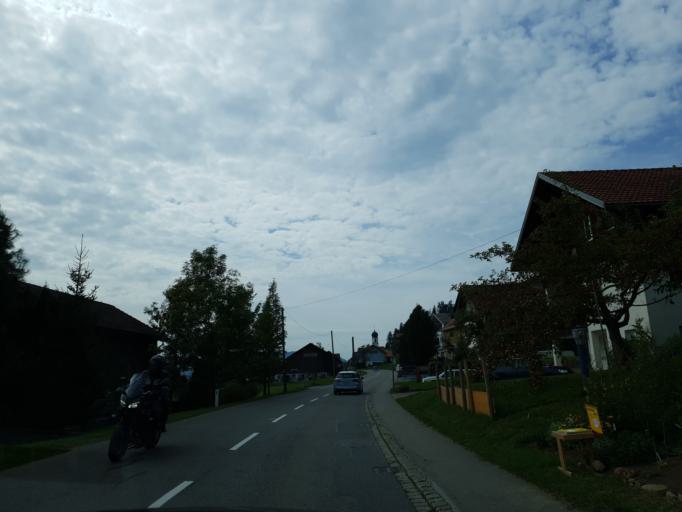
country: AT
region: Vorarlberg
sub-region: Politischer Bezirk Bregenz
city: Doren
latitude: 47.4938
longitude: 9.8857
